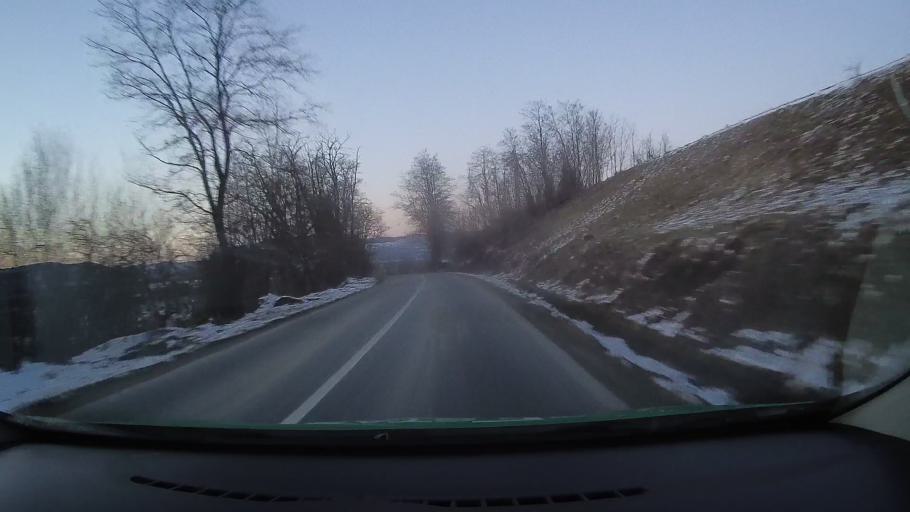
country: RO
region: Sibiu
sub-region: Comuna Alma
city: Alma
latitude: 46.1888
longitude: 24.4706
